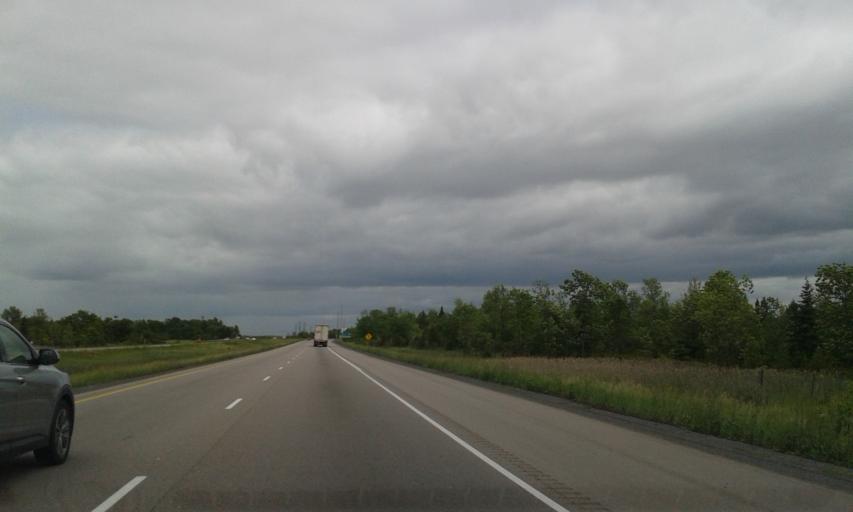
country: CA
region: Ontario
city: Kingston
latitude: 44.2847
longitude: -76.6668
